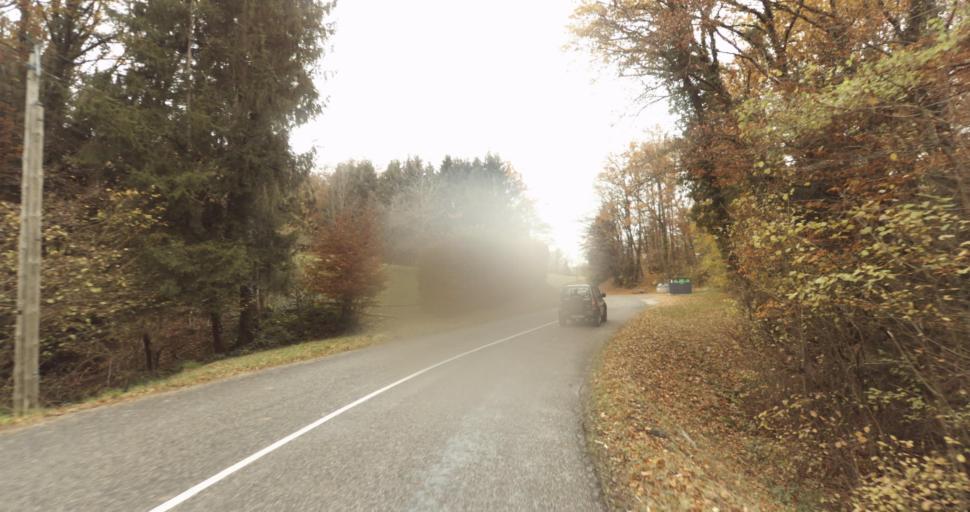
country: FR
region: Rhone-Alpes
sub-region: Departement de la Haute-Savoie
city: Saint-Martin-Bellevue
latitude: 45.9891
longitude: 6.1541
